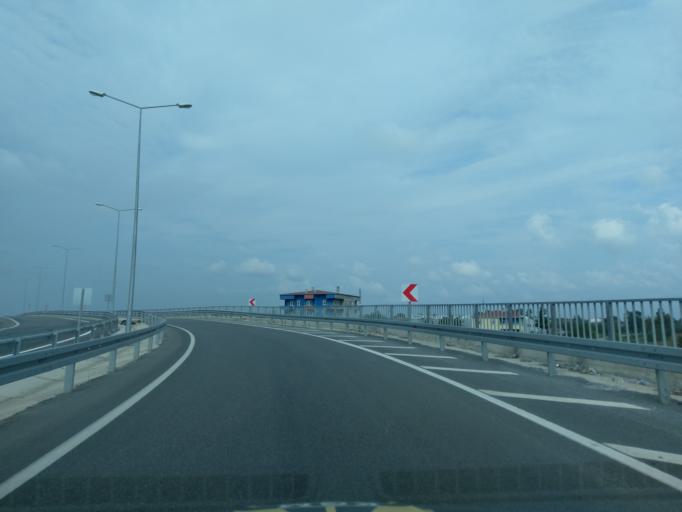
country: TR
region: Samsun
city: Tekkekoy
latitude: 41.2356
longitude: 36.5351
